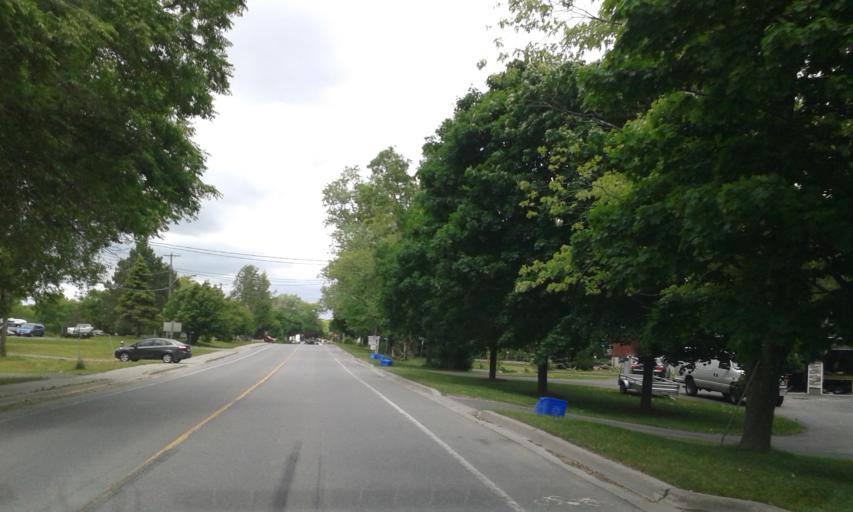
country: CA
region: Ontario
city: Skatepark
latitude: 44.1778
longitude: -76.7837
